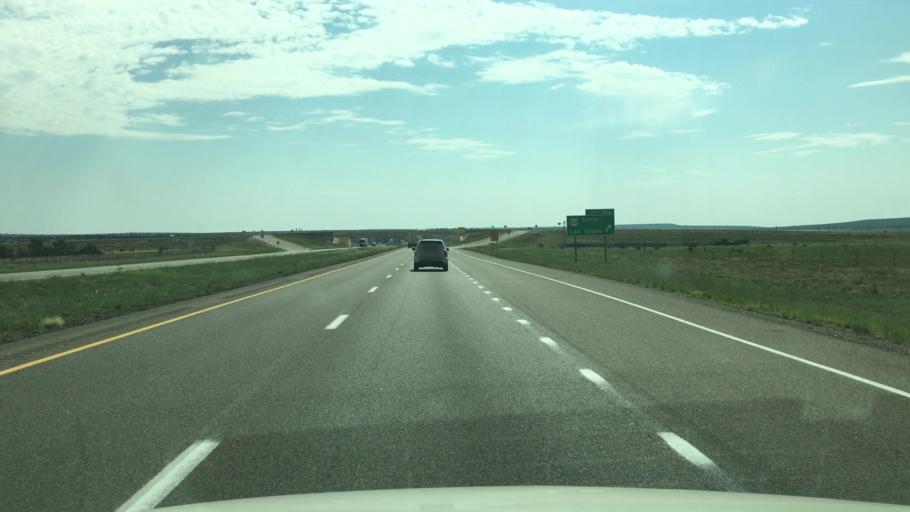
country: US
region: New Mexico
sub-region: Guadalupe County
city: Santa Rosa
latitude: 34.9766
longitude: -104.9968
